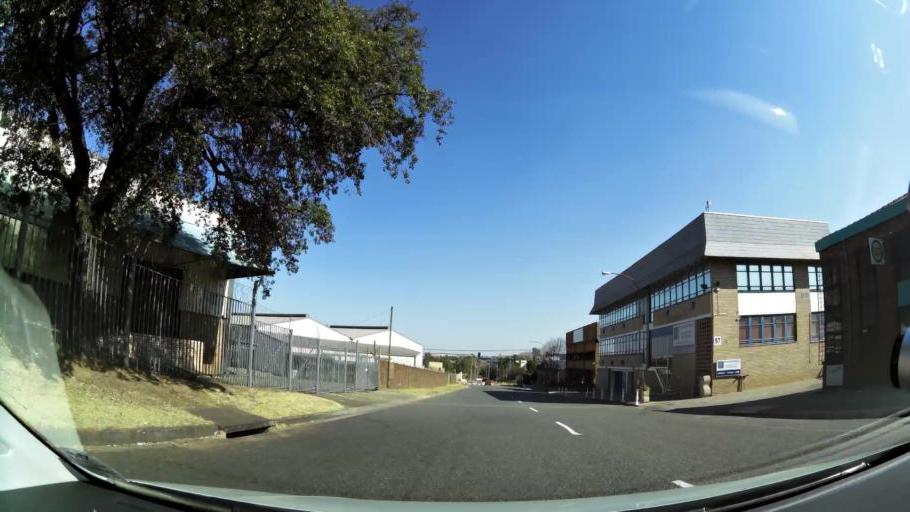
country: ZA
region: Gauteng
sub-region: City of Johannesburg Metropolitan Municipality
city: Johannesburg
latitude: -26.2140
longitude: 28.0323
